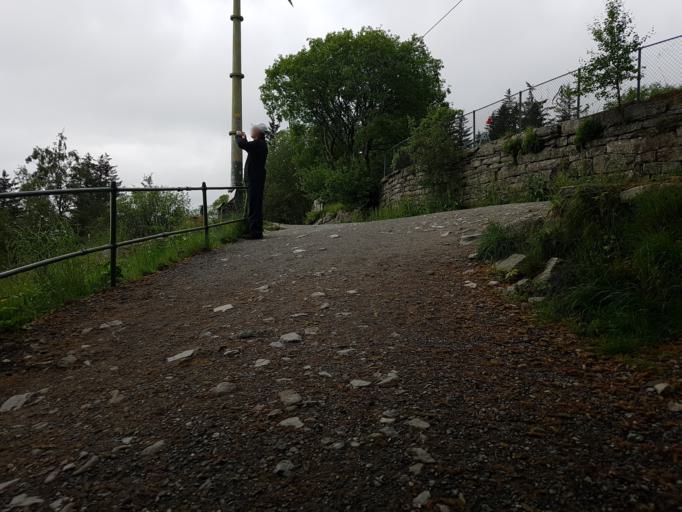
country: NO
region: Hordaland
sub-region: Bergen
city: Bergen
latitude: 60.3975
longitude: 5.3382
